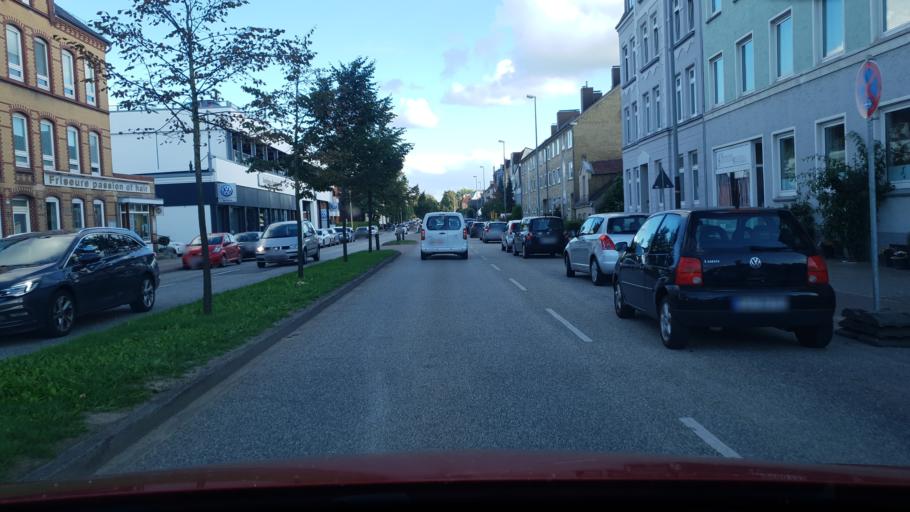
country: DE
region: Schleswig-Holstein
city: Kronshagen
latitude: 54.3428
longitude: 10.1000
